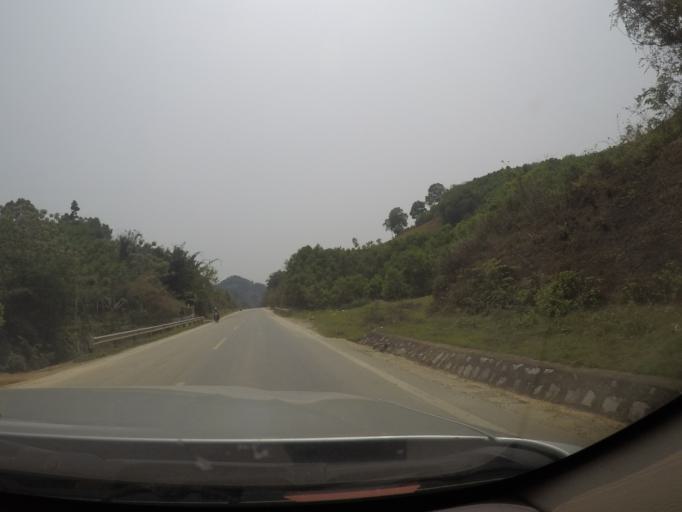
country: VN
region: Thanh Hoa
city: Thi Tran Yen Cat
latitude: 19.6831
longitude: 105.4553
